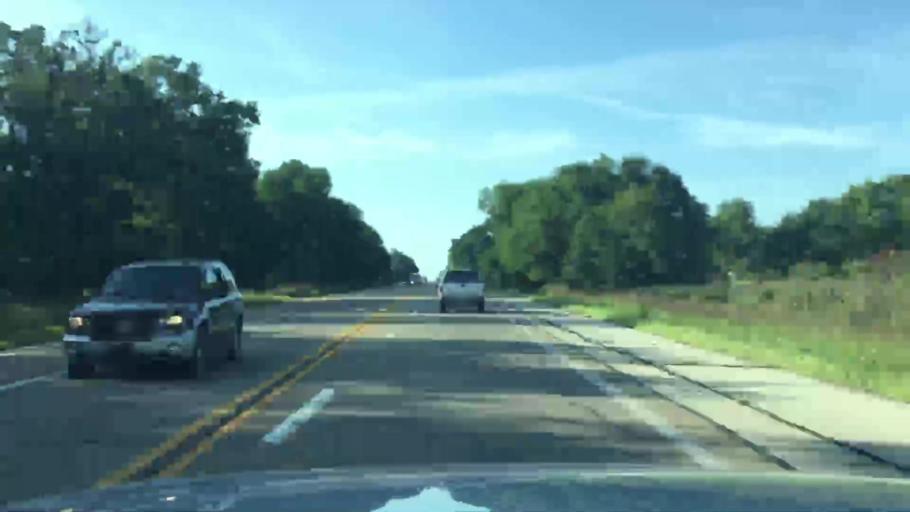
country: US
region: Michigan
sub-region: Jackson County
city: Vandercook Lake
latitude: 42.0919
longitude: -84.3638
